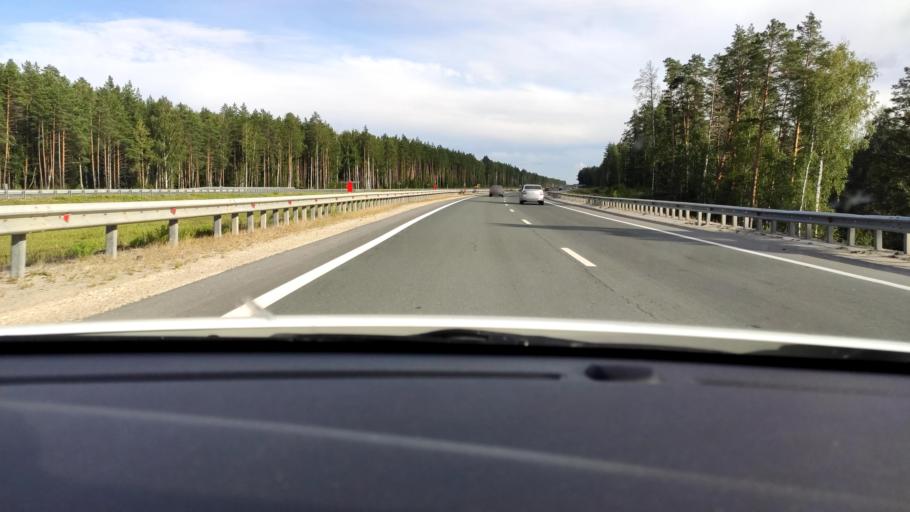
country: RU
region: Mariy-El
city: Surok
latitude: 56.5317
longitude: 48.0012
